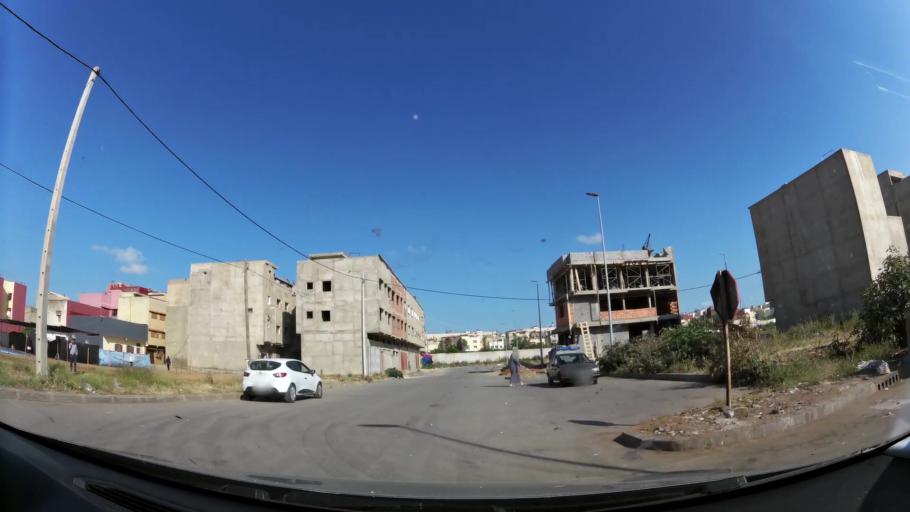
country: MA
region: Rabat-Sale-Zemmour-Zaer
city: Sale
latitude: 34.0493
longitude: -6.8102
